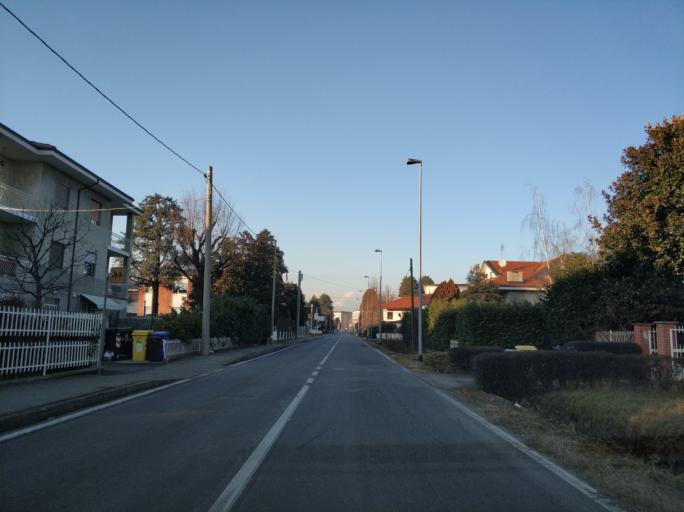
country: IT
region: Piedmont
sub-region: Provincia di Torino
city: San Maurizio
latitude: 45.2104
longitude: 7.6350
